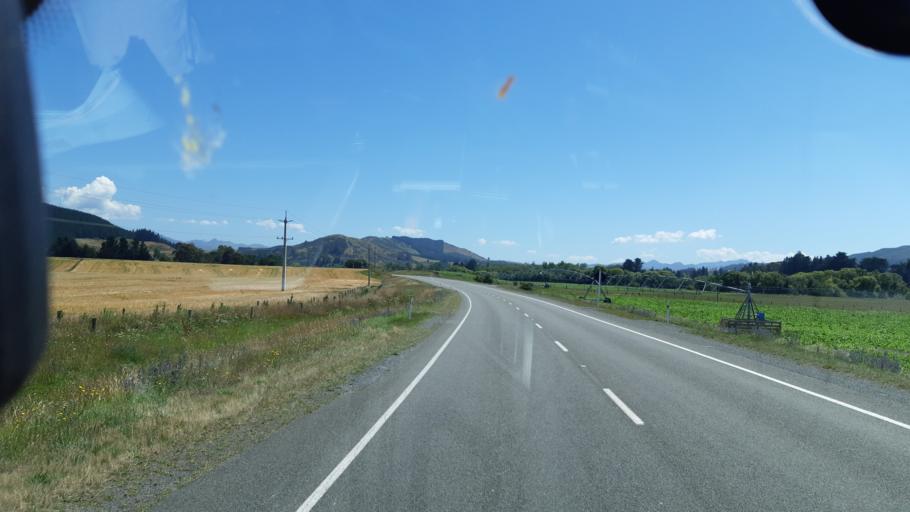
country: NZ
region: Canterbury
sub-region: Kaikoura District
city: Kaikoura
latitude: -42.7003
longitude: 173.3015
